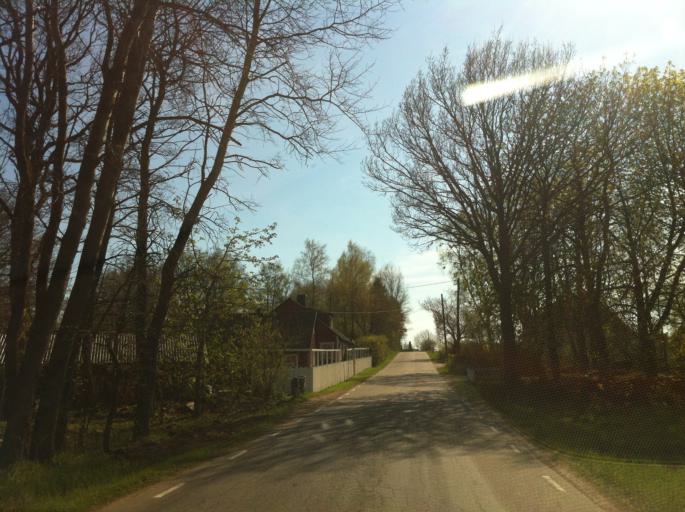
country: SE
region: Skane
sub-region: Svalovs Kommun
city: Kagerod
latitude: 56.0655
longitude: 13.1172
